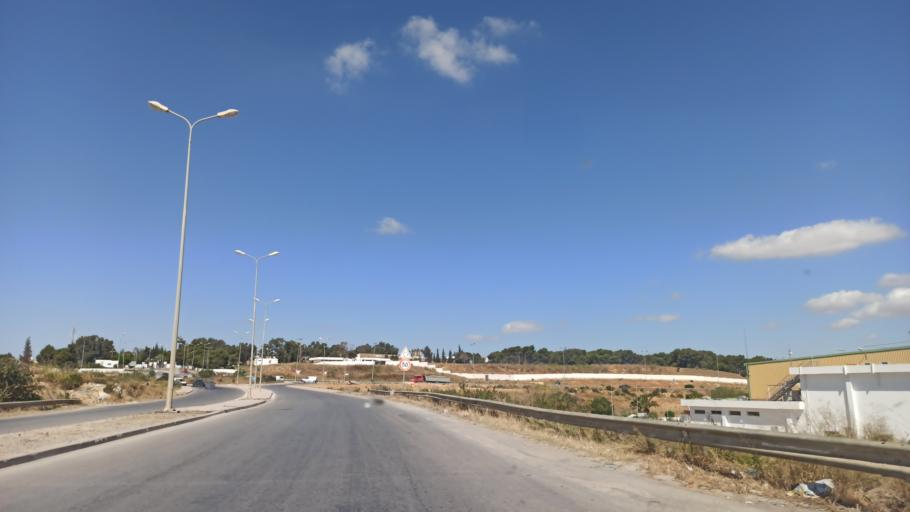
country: TN
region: Manouba
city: Manouba
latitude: 36.7833
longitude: 10.0743
